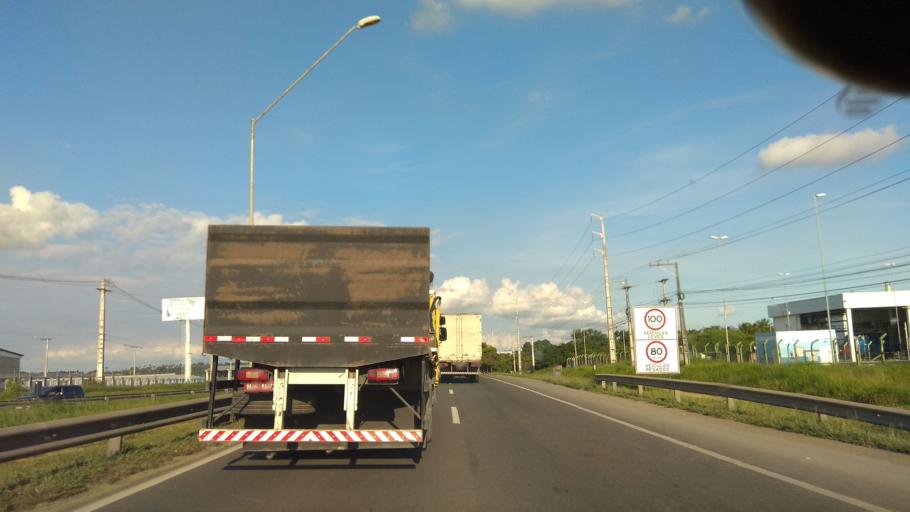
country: BR
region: Bahia
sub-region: Conceicao Do Jacuipe
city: Conceicao do Jacuipe
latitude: -12.3200
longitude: -38.8724
